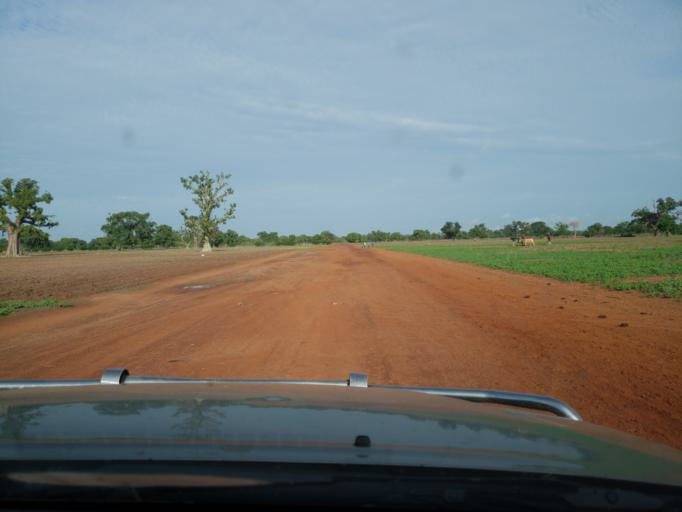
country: ML
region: Sikasso
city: Koutiala
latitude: 12.4209
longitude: -5.6933
